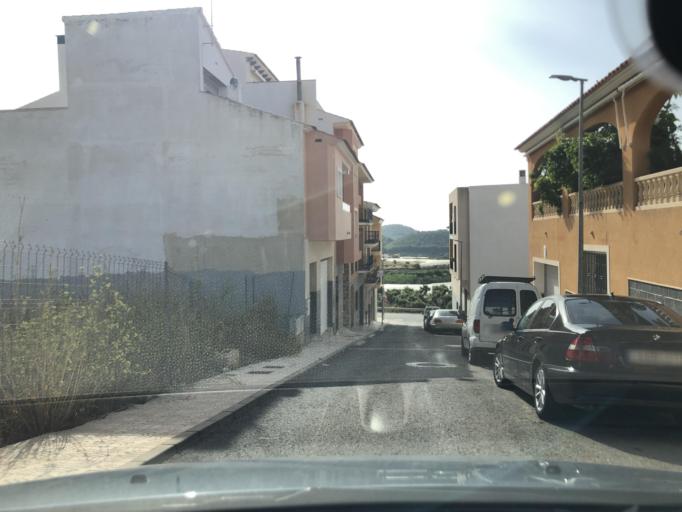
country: ES
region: Valencia
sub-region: Provincia de Alicante
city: Callosa d'En Sarria
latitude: 38.6522
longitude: -0.1284
